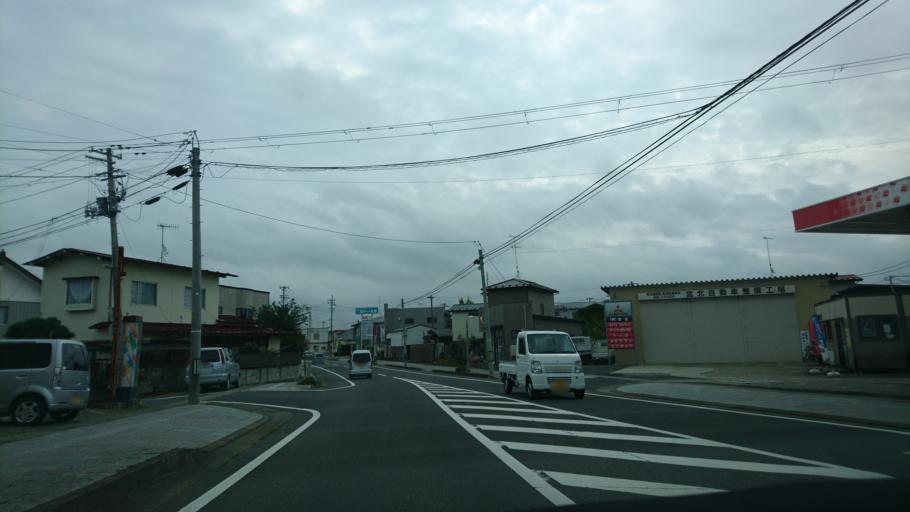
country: JP
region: Iwate
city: Ichinoseki
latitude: 38.7711
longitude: 141.1330
